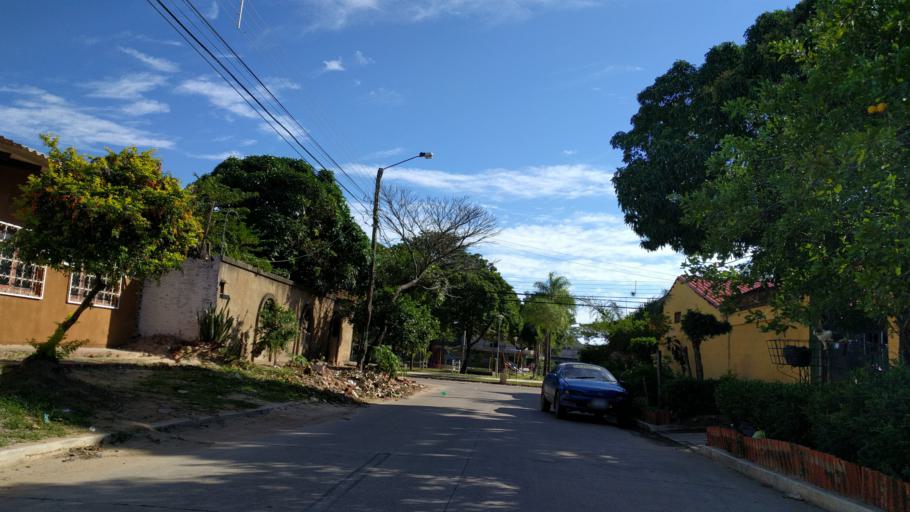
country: BO
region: Santa Cruz
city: Santa Cruz de la Sierra
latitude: -17.7960
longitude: -63.2192
